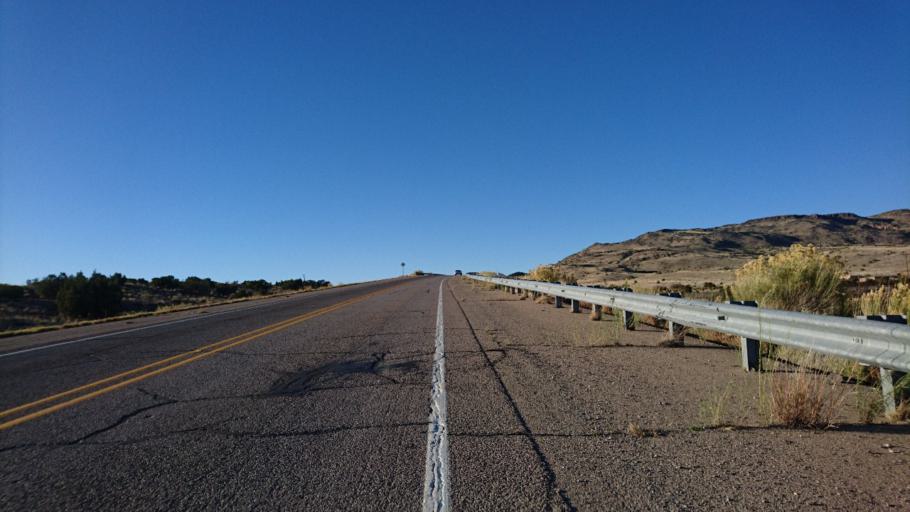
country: US
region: New Mexico
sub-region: Cibola County
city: Grants
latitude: 35.1044
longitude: -107.7788
